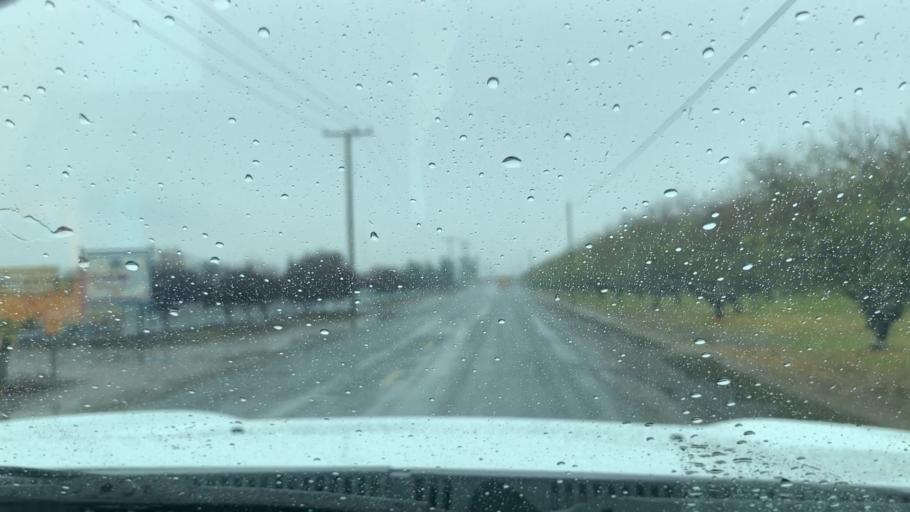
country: US
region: California
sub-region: Tulare County
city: Earlimart
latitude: 35.8339
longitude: -119.2527
